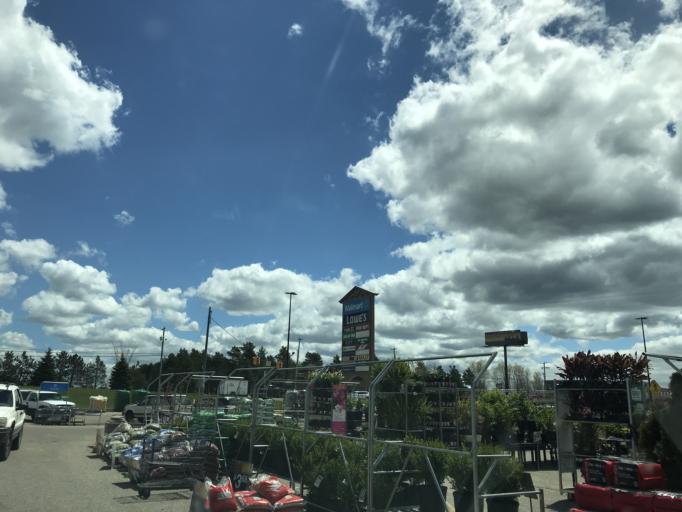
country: US
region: Michigan
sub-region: Otsego County
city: Gaylord
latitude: 45.0236
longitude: -84.6889
